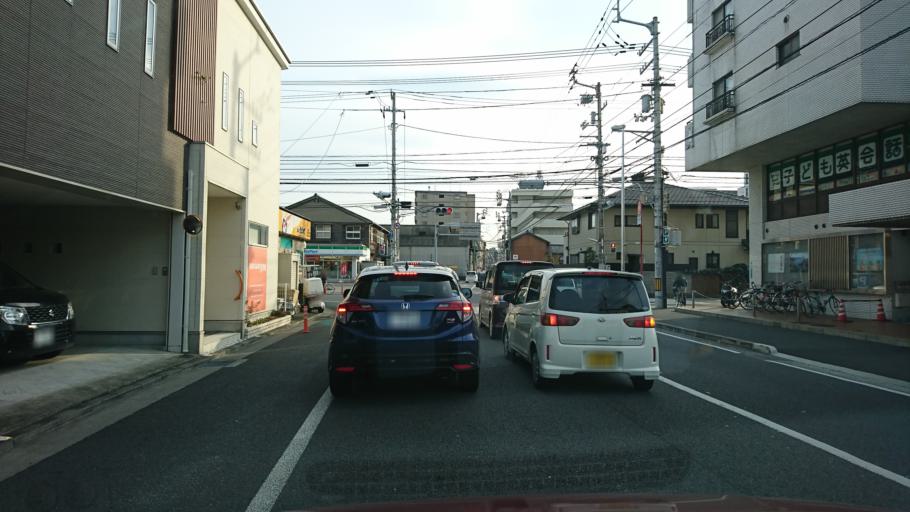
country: JP
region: Ehime
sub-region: Shikoku-chuo Shi
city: Matsuyama
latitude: 33.8525
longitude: 132.7763
